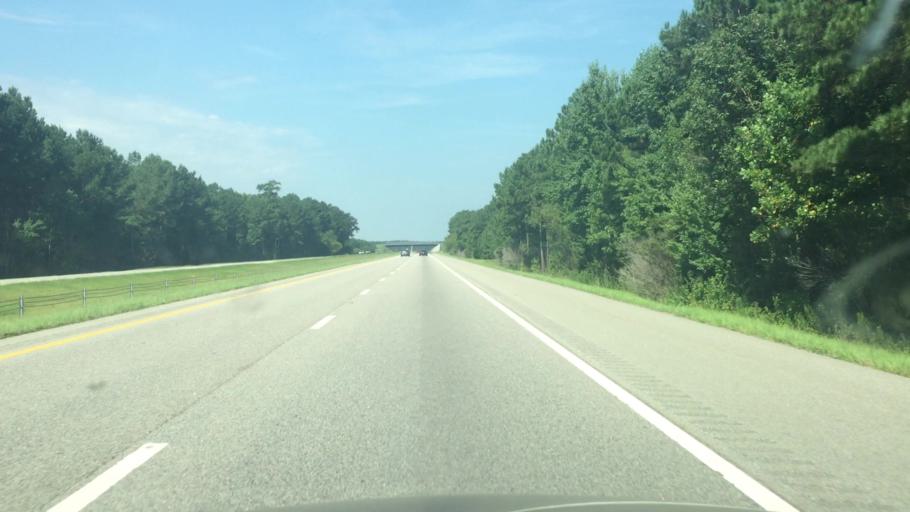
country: US
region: North Carolina
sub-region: Robeson County
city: Pembroke
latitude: 34.5970
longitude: -79.1604
